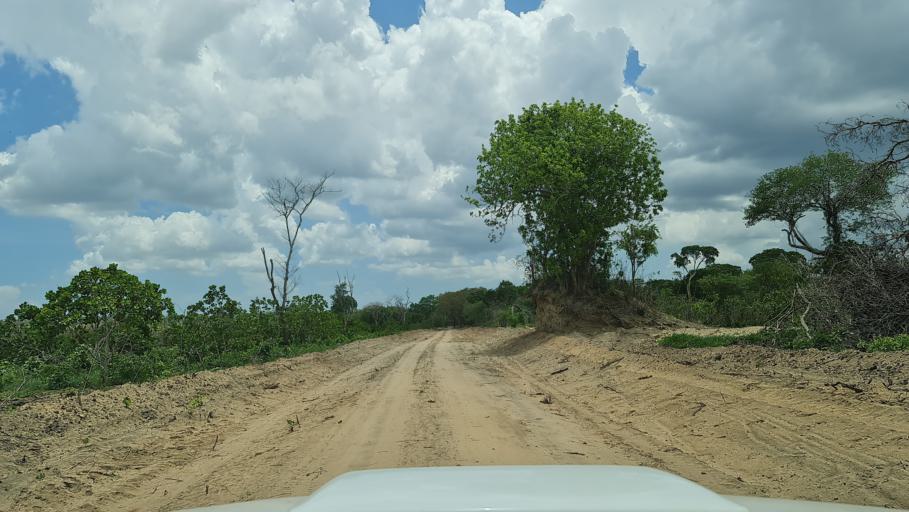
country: MZ
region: Nampula
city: Ilha de Mocambique
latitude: -15.2472
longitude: 40.3675
